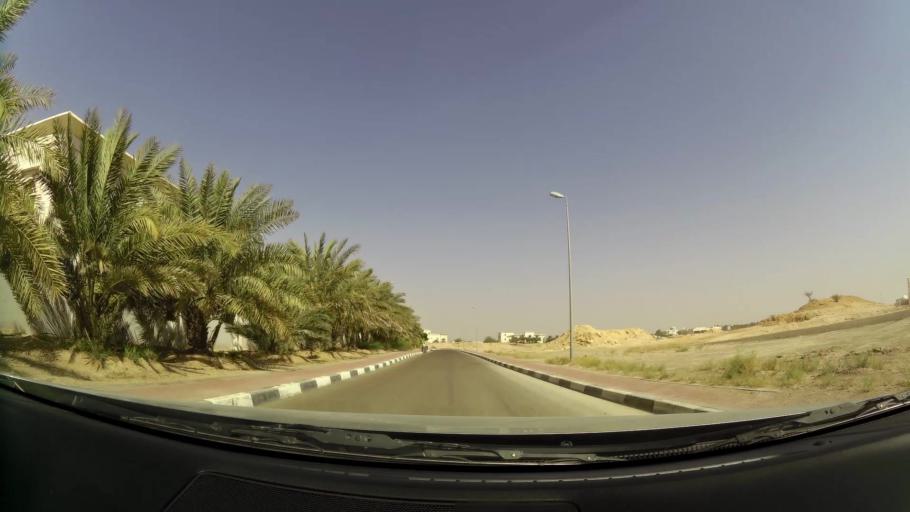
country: OM
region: Al Buraimi
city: Al Buraymi
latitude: 24.3166
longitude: 55.8096
